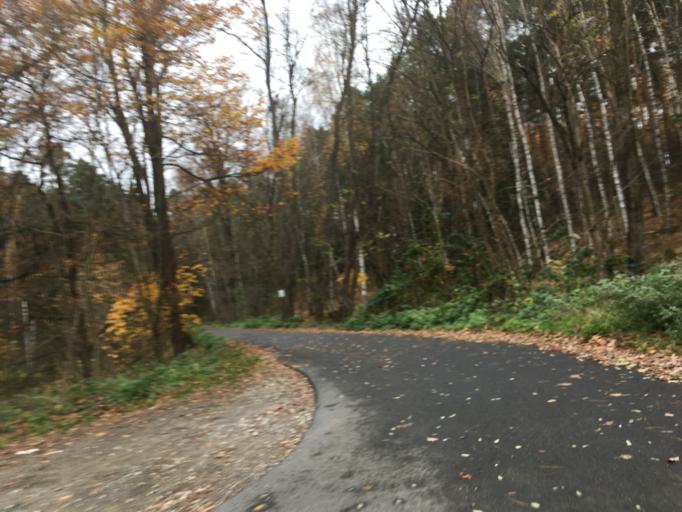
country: DE
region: Brandenburg
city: Mullrose
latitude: 52.2228
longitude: 14.4425
